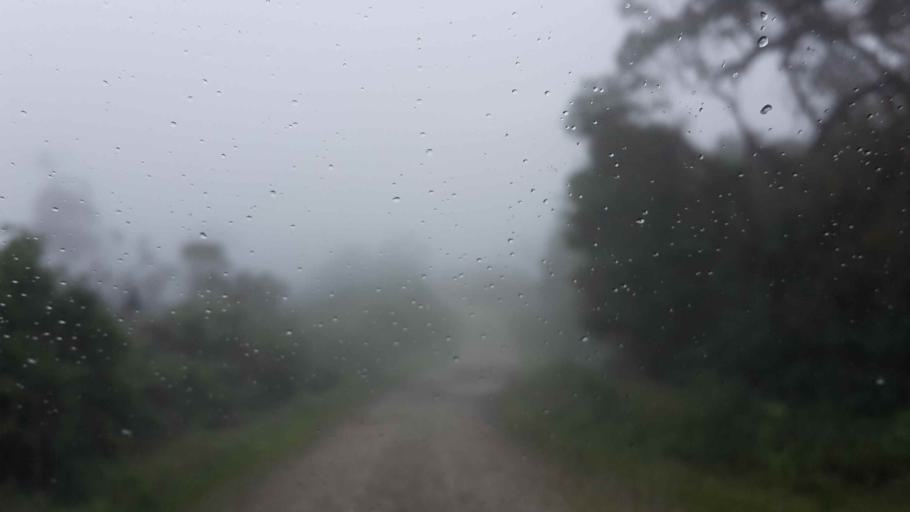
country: BO
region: Cochabamba
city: Colomi
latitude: -17.1231
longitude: -65.9647
